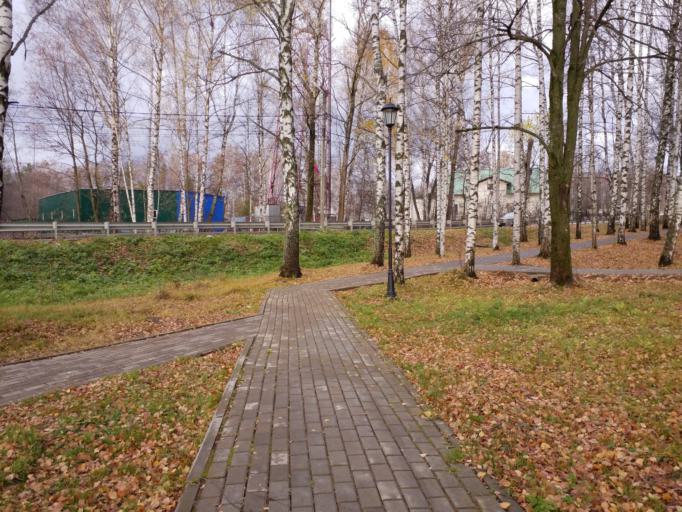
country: RU
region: Moskovskaya
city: Ashukino
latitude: 56.1612
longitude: 37.9432
